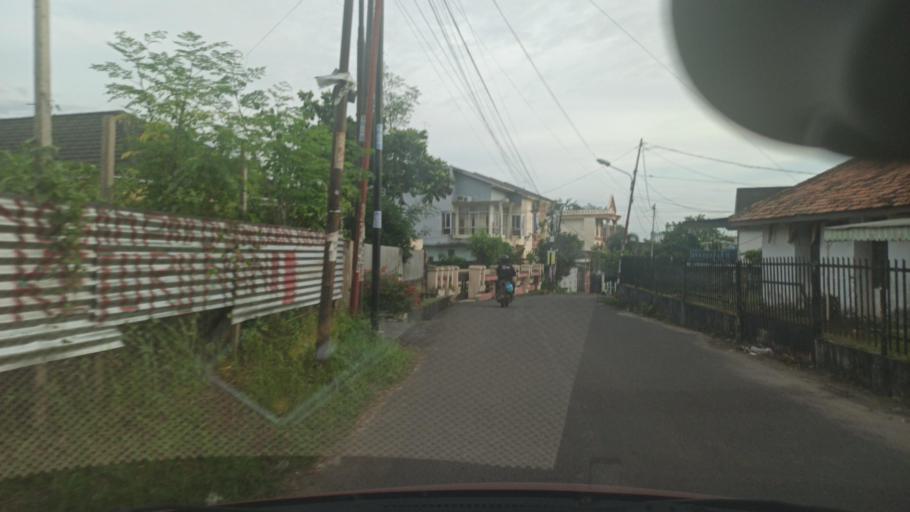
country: ID
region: South Sumatra
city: Palembang
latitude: -2.9603
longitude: 104.7297
